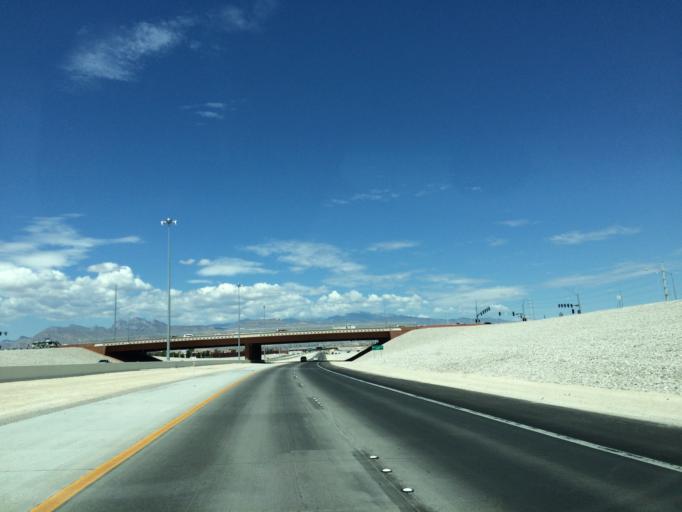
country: US
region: Nevada
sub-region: Clark County
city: North Las Vegas
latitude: 36.2755
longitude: -115.2042
